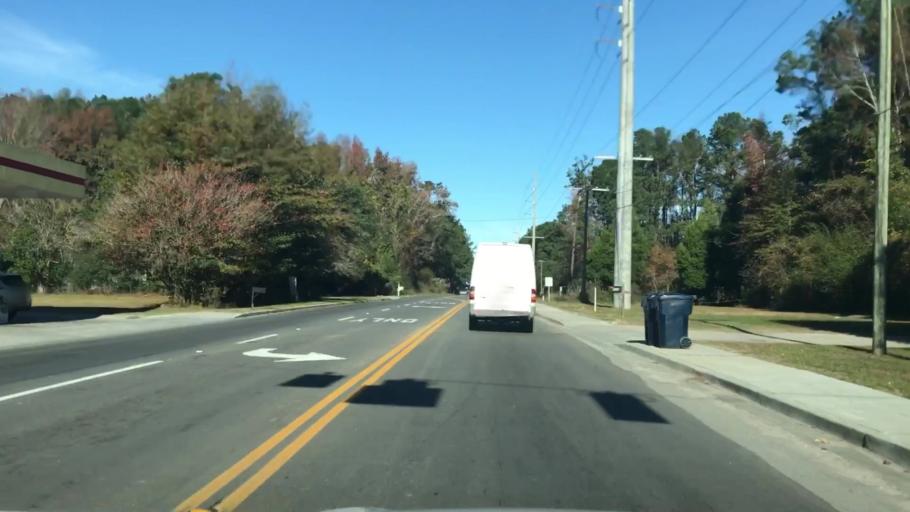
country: US
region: South Carolina
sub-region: Dorchester County
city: Summerville
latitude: 32.9967
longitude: -80.2283
